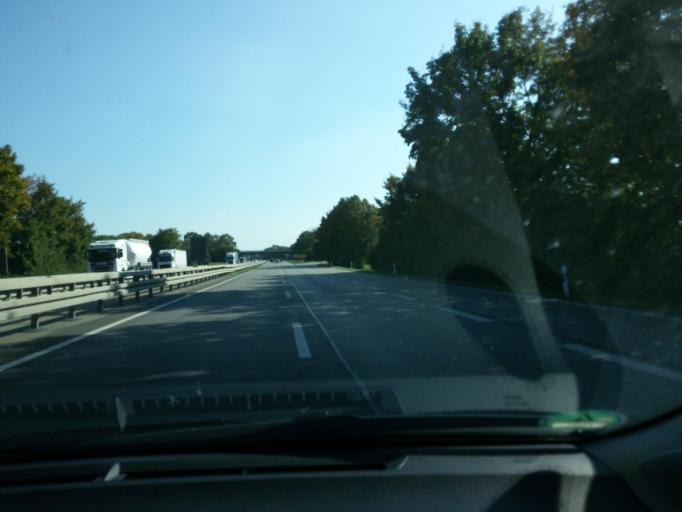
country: DE
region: Bavaria
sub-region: Swabia
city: Asbach-Baumenheim
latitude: 48.7058
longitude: 10.8051
